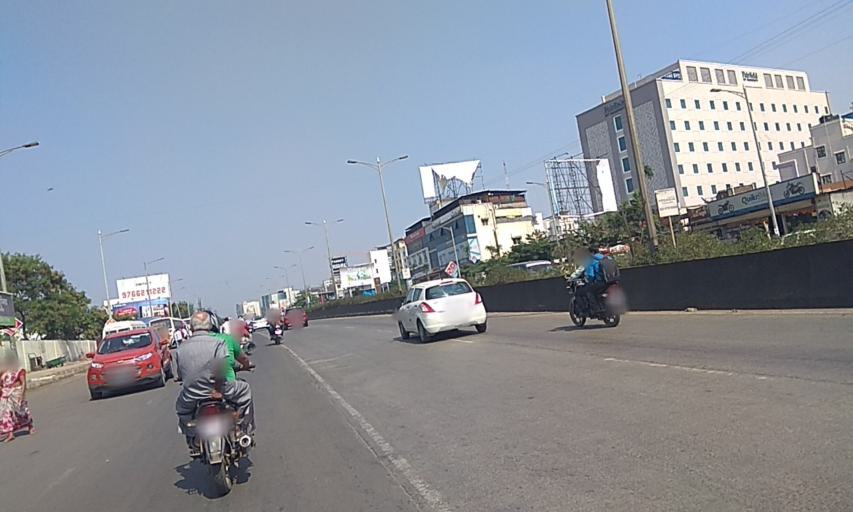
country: IN
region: Maharashtra
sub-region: Pune Division
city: Lohogaon
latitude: 18.5453
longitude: 73.9358
